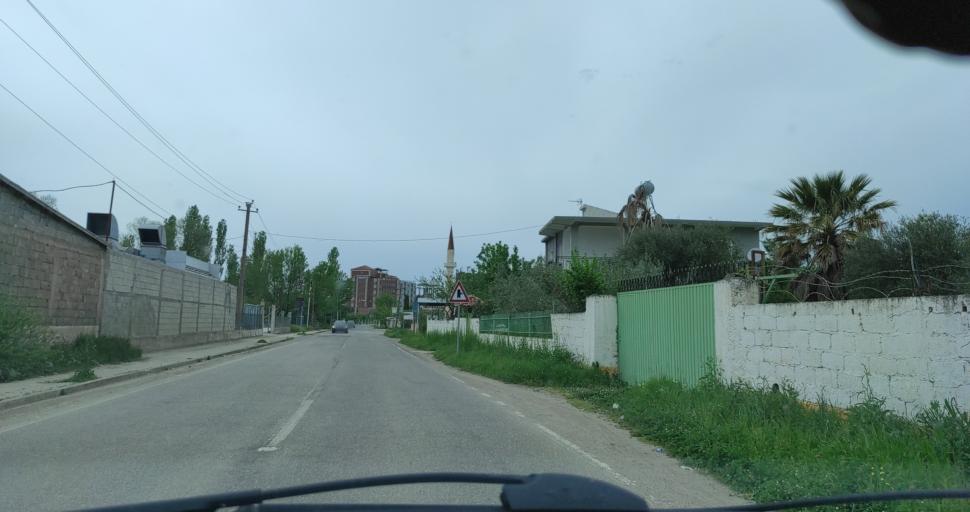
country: AL
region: Lezhe
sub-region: Rrethi i Kurbinit
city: Lac
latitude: 41.6184
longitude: 19.7115
